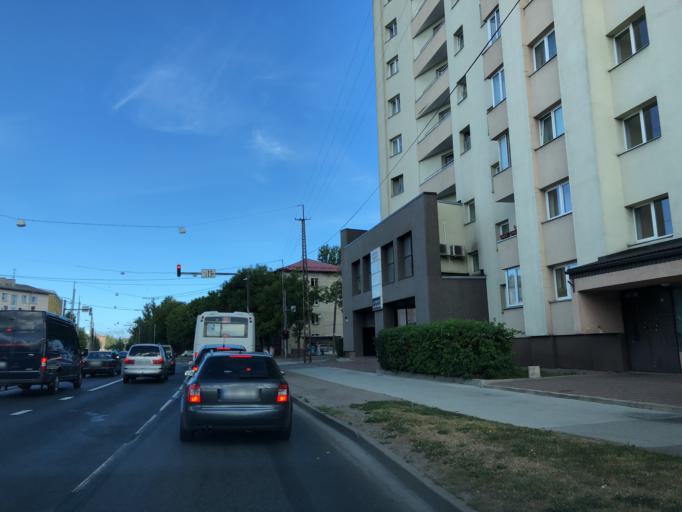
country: EE
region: Harju
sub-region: Tallinna linn
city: Tallinn
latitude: 59.4485
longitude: 24.6987
